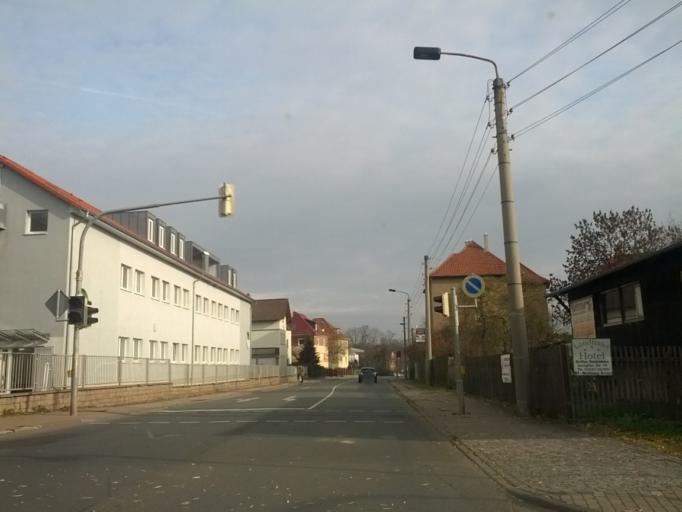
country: DE
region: Thuringia
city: Gotha
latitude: 50.9387
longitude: 10.6937
